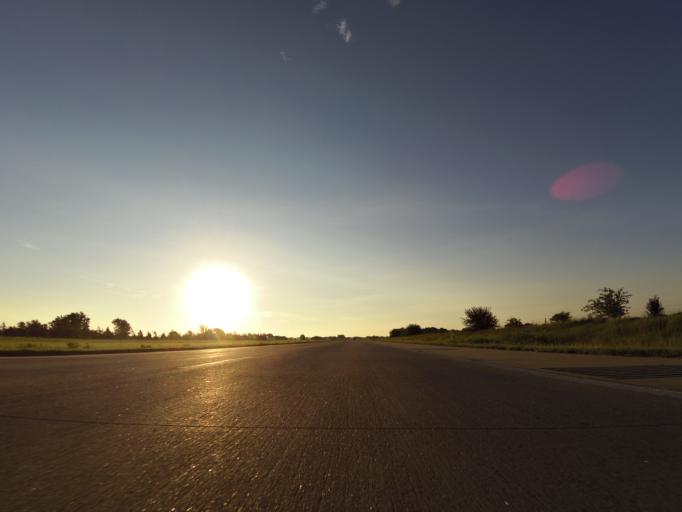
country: US
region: Kansas
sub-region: Reno County
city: Haven
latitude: 37.8940
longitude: -97.7702
